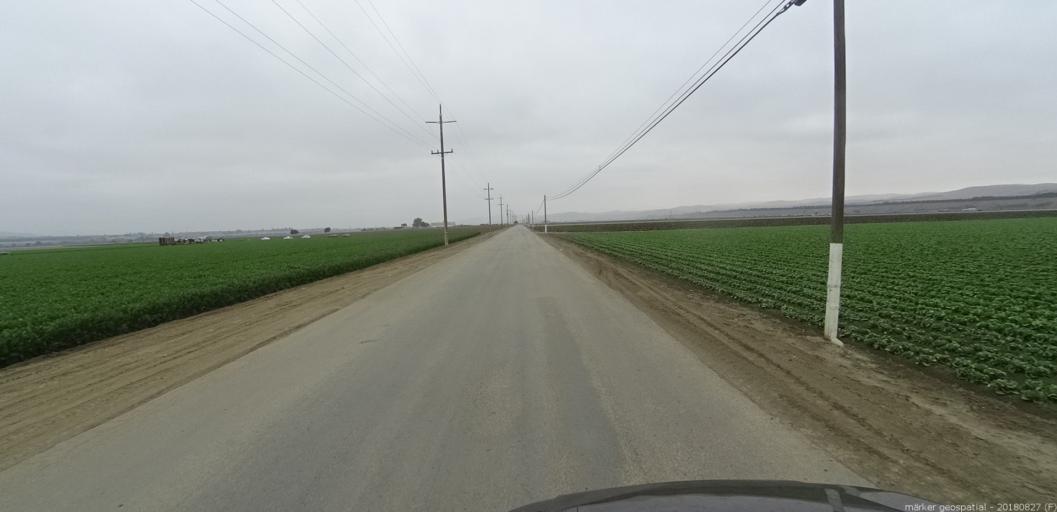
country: US
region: California
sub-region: Monterey County
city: King City
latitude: 36.2376
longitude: -121.1443
